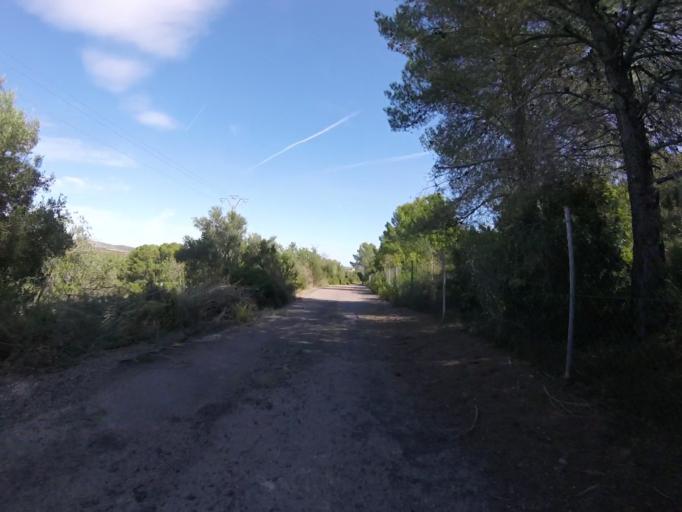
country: ES
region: Valencia
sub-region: Provincia de Castello
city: Santa Magdalena de Pulpis
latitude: 40.3901
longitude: 0.3505
